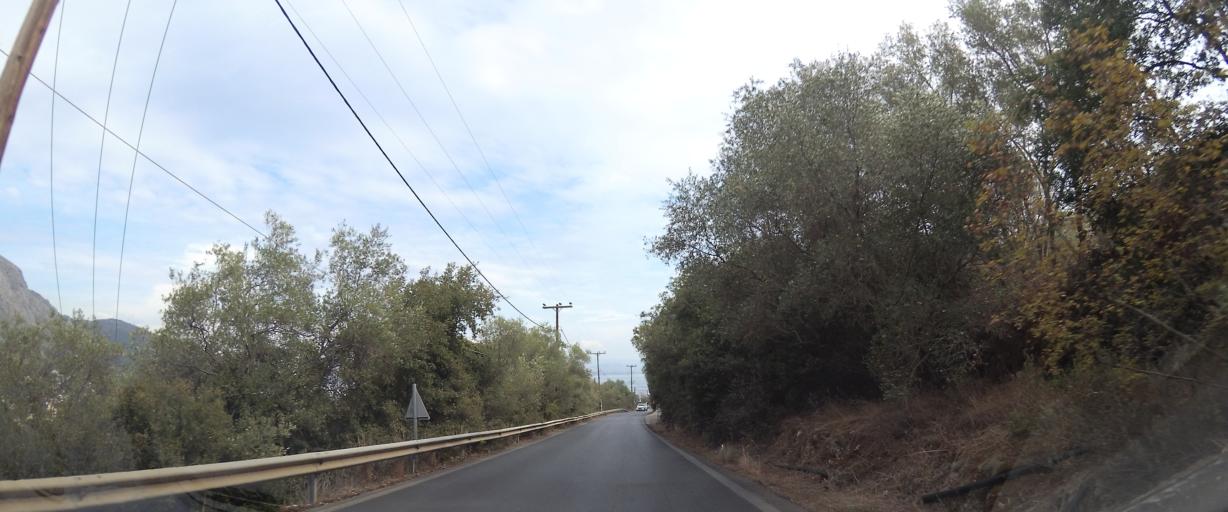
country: GR
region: Ionian Islands
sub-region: Nomos Kerkyras
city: Kontokali
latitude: 39.7123
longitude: 19.8604
